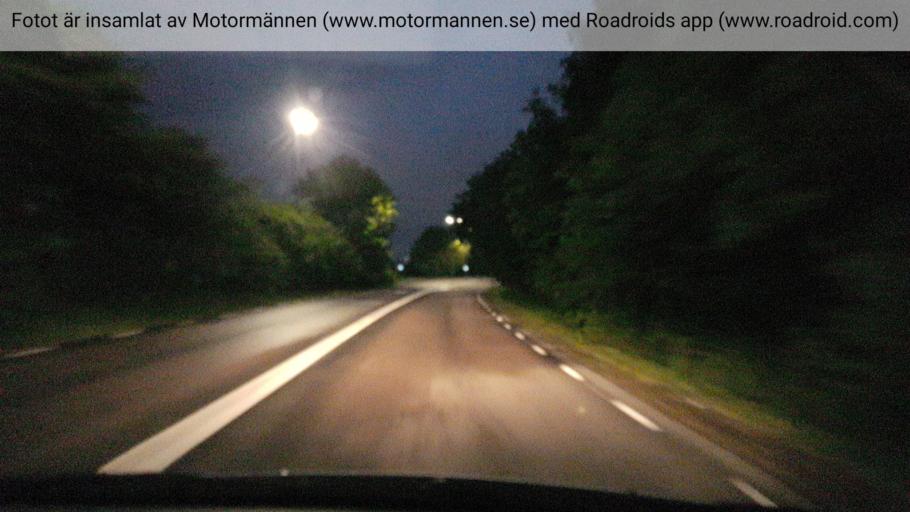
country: SE
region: Vaestmanland
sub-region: Vasteras
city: Vasteras
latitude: 59.6468
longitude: 16.5316
